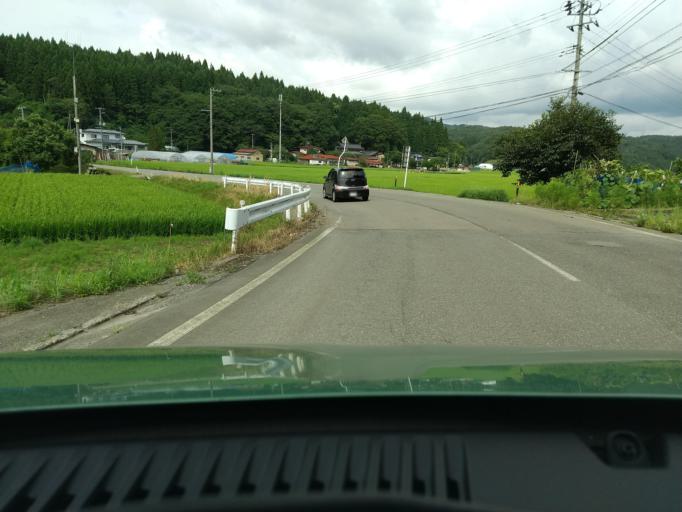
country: JP
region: Akita
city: Akita
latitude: 39.7792
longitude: 140.1346
